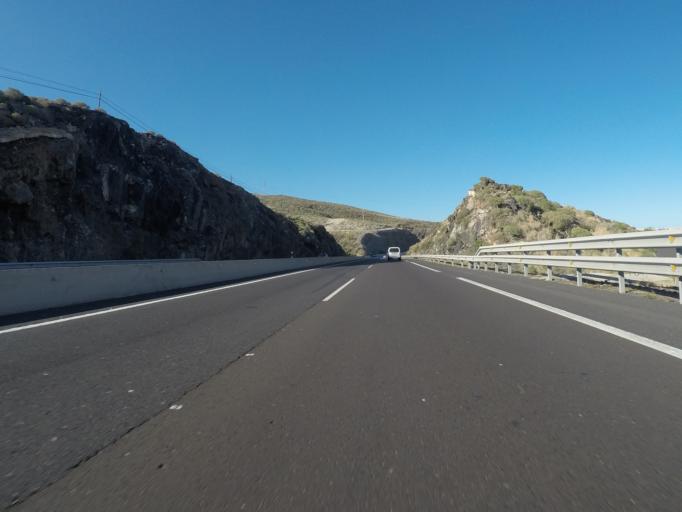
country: ES
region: Canary Islands
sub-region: Provincia de Santa Cruz de Tenerife
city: Fasnia
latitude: 28.2564
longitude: -16.3959
